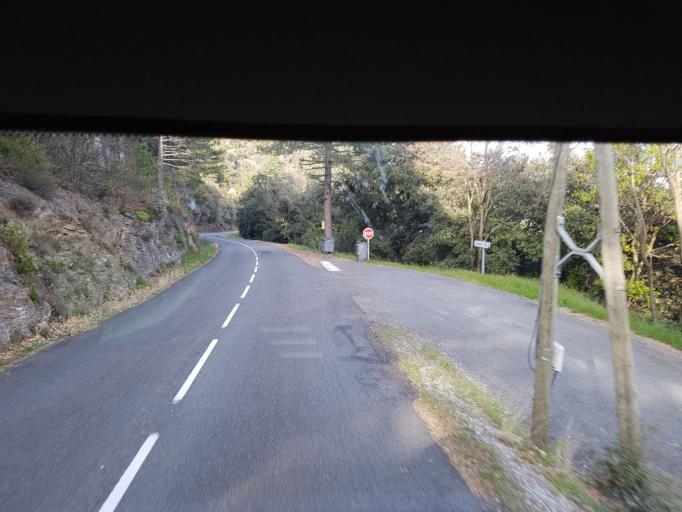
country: FR
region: Languedoc-Roussillon
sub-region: Departement du Gard
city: Branoux-les-Taillades
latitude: 44.3315
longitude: 3.9422
